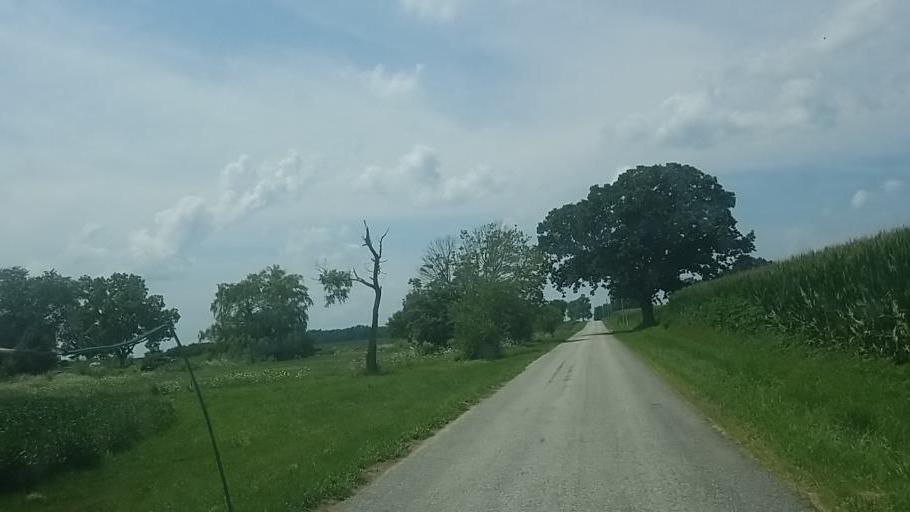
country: US
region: Ohio
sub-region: Marion County
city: Marion
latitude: 40.6733
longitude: -83.2406
